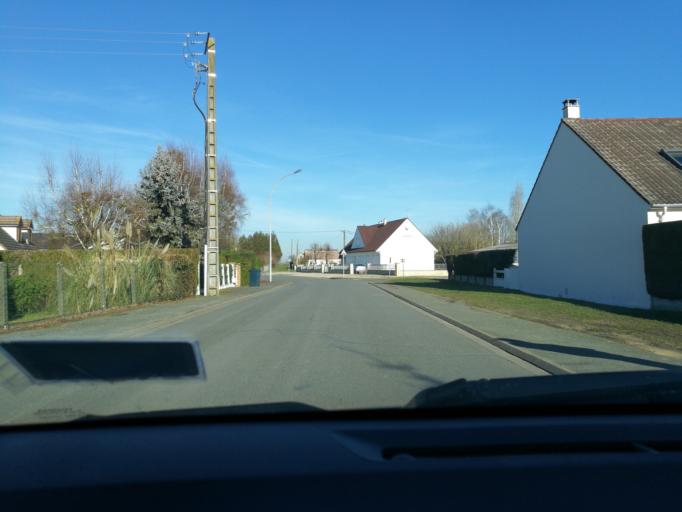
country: FR
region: Centre
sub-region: Departement du Loiret
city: Chaingy
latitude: 47.8814
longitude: 1.7698
